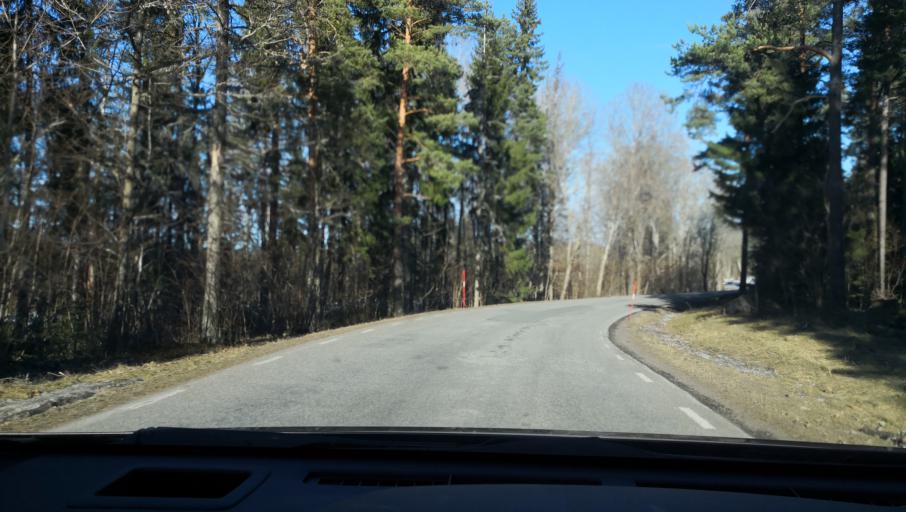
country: SE
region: Uppsala
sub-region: Osthammars Kommun
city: Osterbybruk
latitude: 60.2100
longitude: 17.9034
